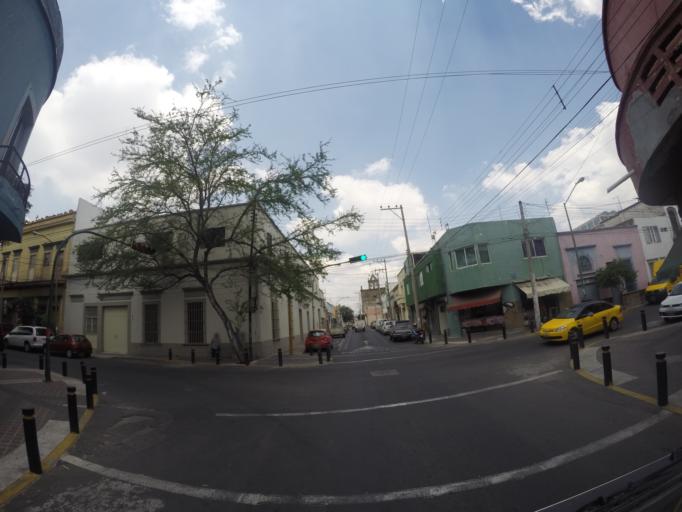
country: MX
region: Jalisco
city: Guadalajara
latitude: 20.6811
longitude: -103.3490
